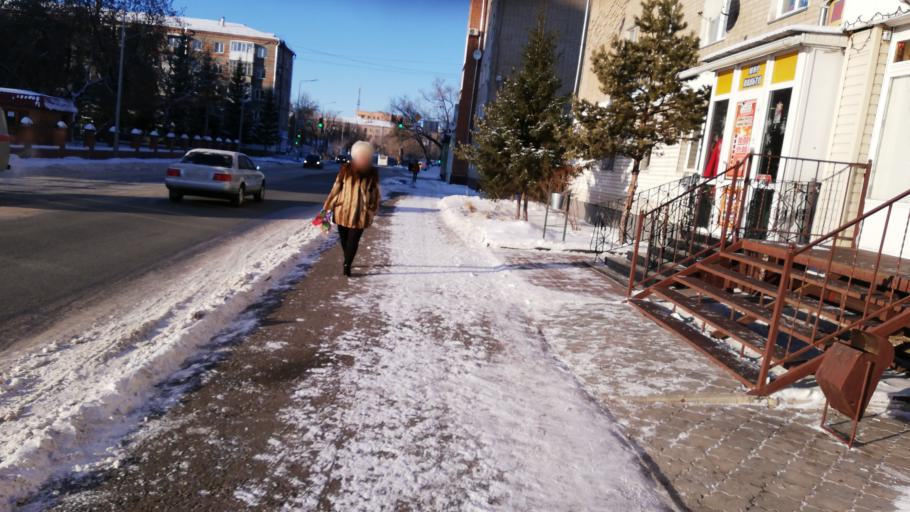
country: KZ
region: Soltustik Qazaqstan
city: Petropavlovsk
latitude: 54.8642
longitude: 69.1414
